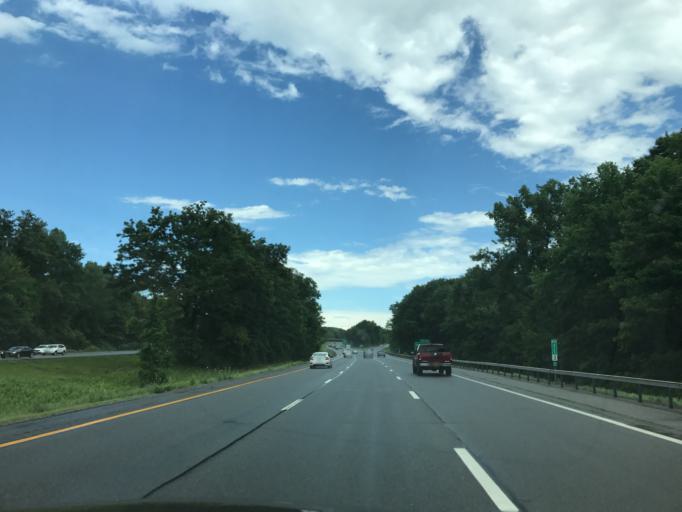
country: US
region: New York
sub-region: Saratoga County
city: Country Knolls
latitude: 42.8339
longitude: -73.7698
